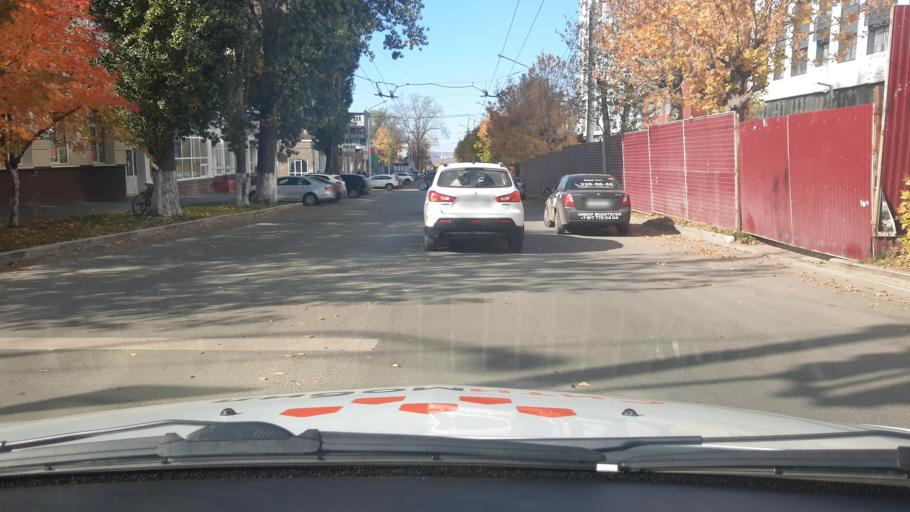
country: RU
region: Bashkortostan
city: Ufa
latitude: 54.7291
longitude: 55.9296
